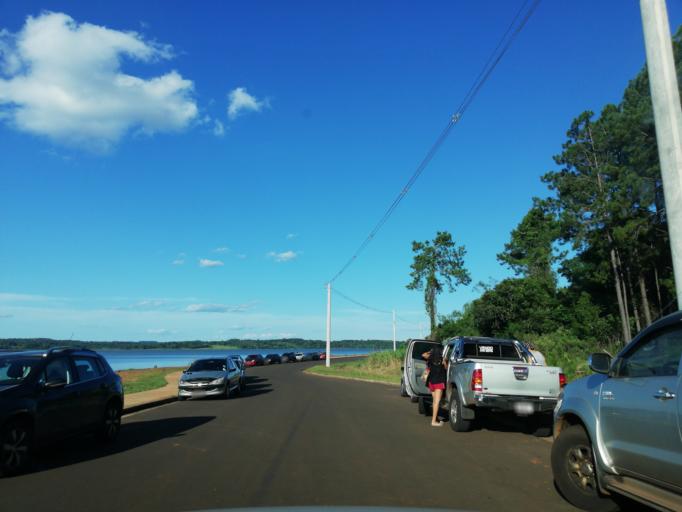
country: AR
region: Misiones
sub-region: Departamento de Candelaria
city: Candelaria
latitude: -27.4515
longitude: -55.7808
